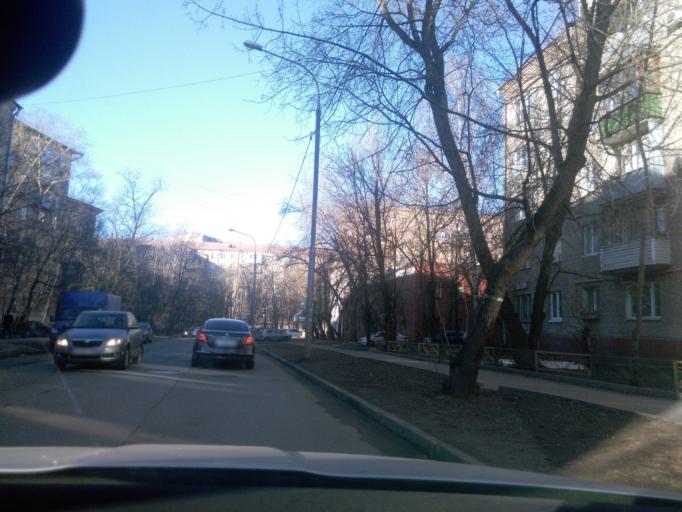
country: RU
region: Moskovskaya
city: Koptevo
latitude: 55.8176
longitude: 37.5122
